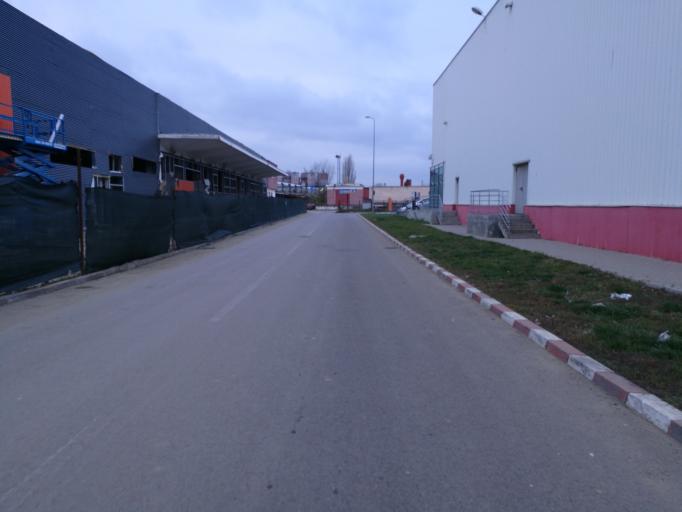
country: RO
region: Suceava
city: Suceava
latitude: 47.6640
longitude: 26.2652
